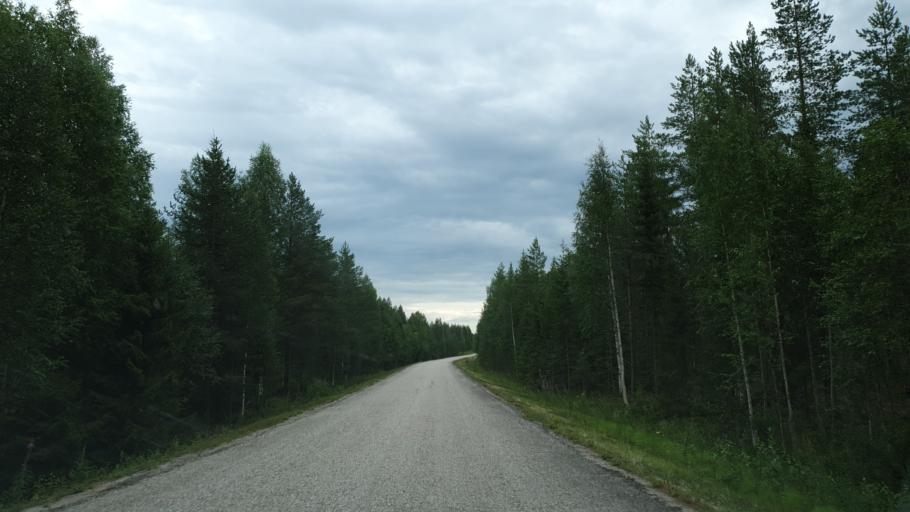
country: FI
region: Kainuu
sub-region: Kehys-Kainuu
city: Kuhmo
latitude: 64.3445
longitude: 29.2834
